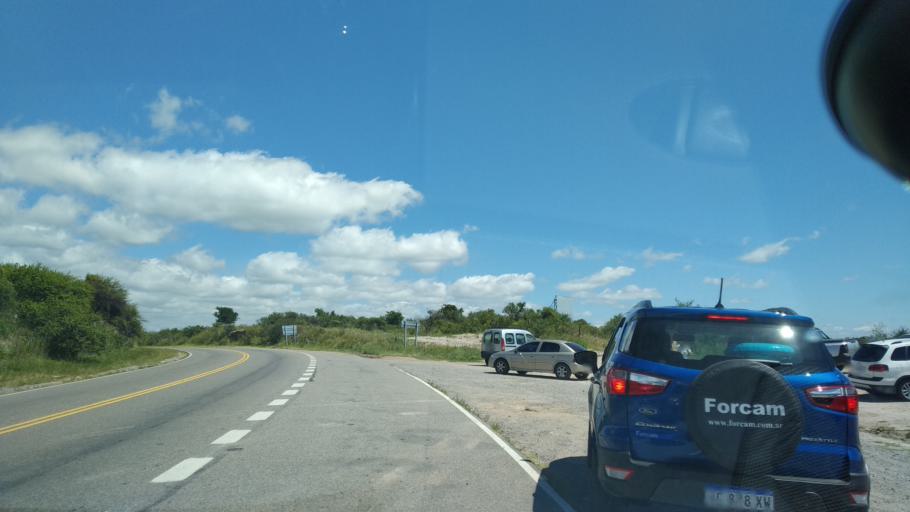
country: AR
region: Cordoba
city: Villa Cura Brochero
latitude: -31.6945
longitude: -65.0603
